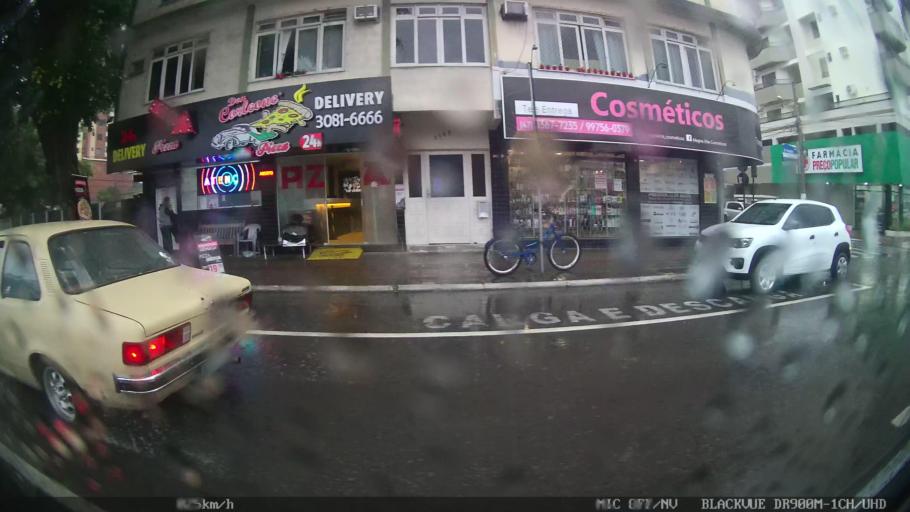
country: BR
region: Santa Catarina
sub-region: Balneario Camboriu
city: Balneario Camboriu
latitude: -26.9946
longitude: -48.6354
